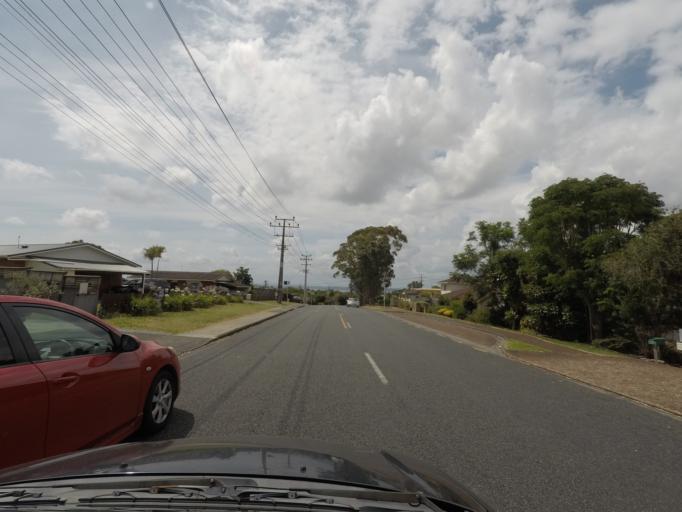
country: NZ
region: Auckland
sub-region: Auckland
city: Waitakere
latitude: -36.8988
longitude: 174.6429
